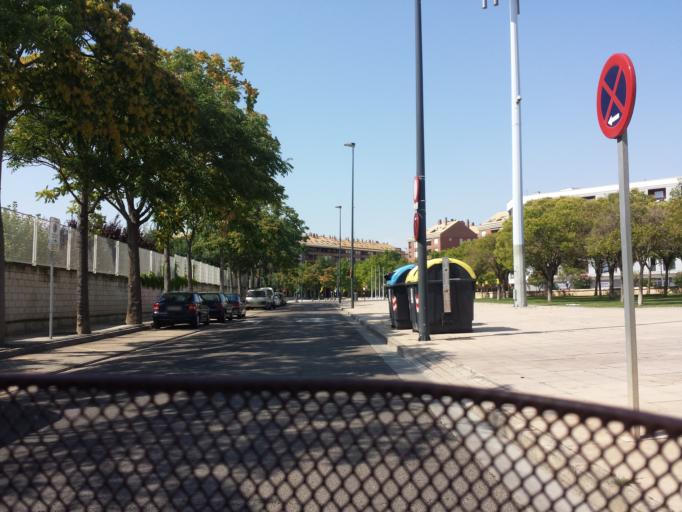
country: ES
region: Aragon
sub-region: Provincia de Zaragoza
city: Zaragoza
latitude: 41.6357
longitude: -0.8672
